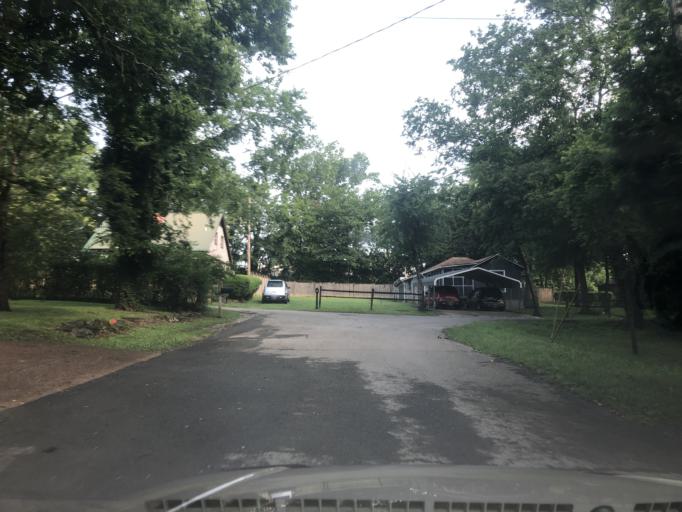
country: US
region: Tennessee
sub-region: Davidson County
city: Lakewood
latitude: 36.2443
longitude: -86.7114
